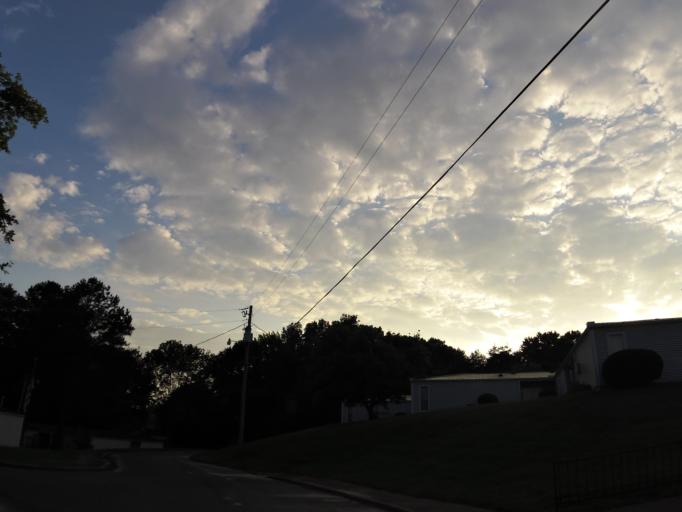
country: US
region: Tennessee
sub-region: Henry County
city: Paris
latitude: 36.2920
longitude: -88.3118
